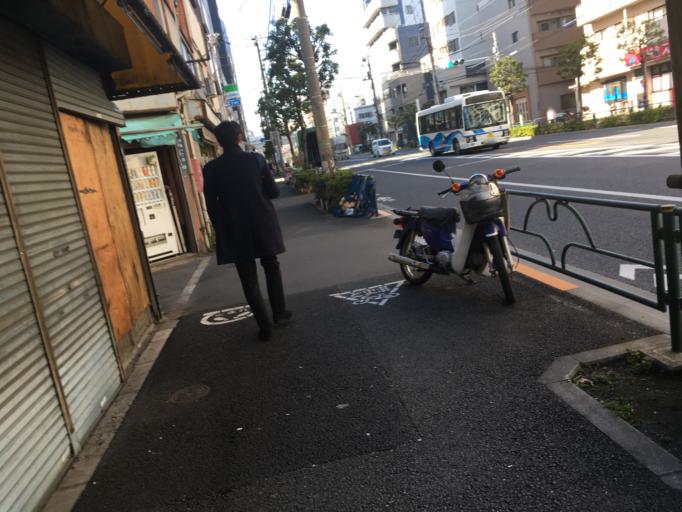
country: JP
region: Tokyo
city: Urayasu
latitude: 35.7179
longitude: 139.8227
